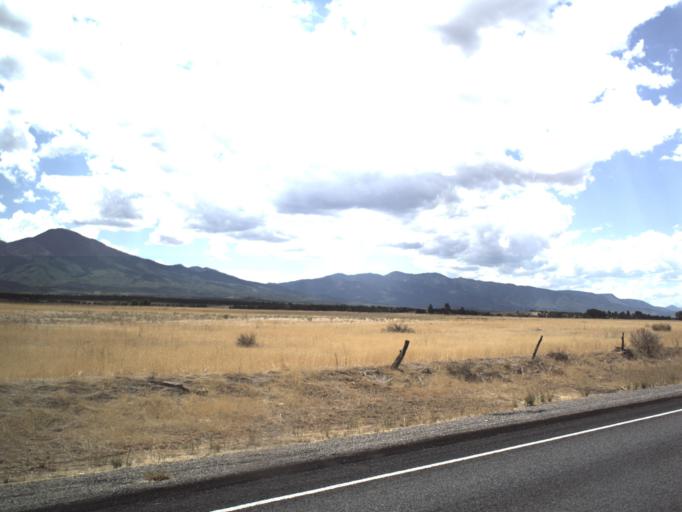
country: US
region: Utah
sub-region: Millard County
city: Fillmore
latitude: 39.1196
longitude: -112.2596
